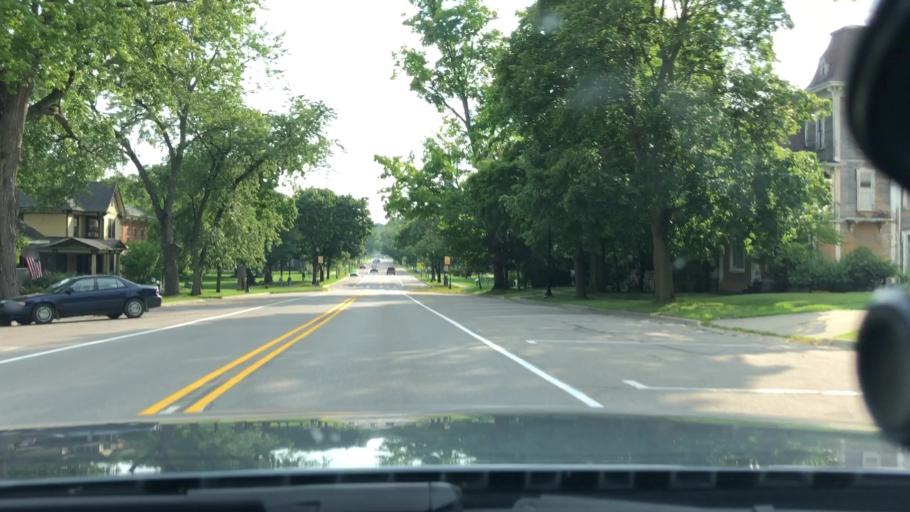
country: US
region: Michigan
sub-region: Washtenaw County
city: Manchester
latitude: 42.1493
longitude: -84.0403
